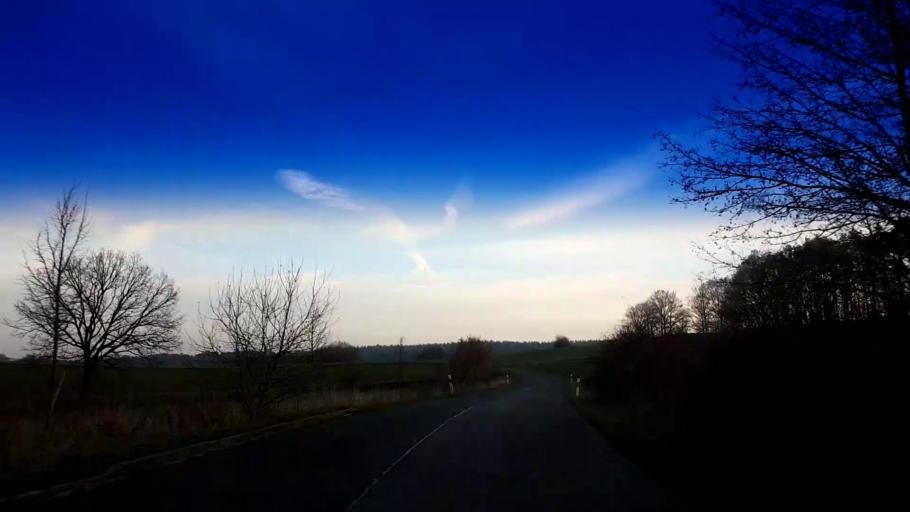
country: DE
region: Bavaria
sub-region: Upper Franconia
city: Stegaurach
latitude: 49.8637
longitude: 10.8200
